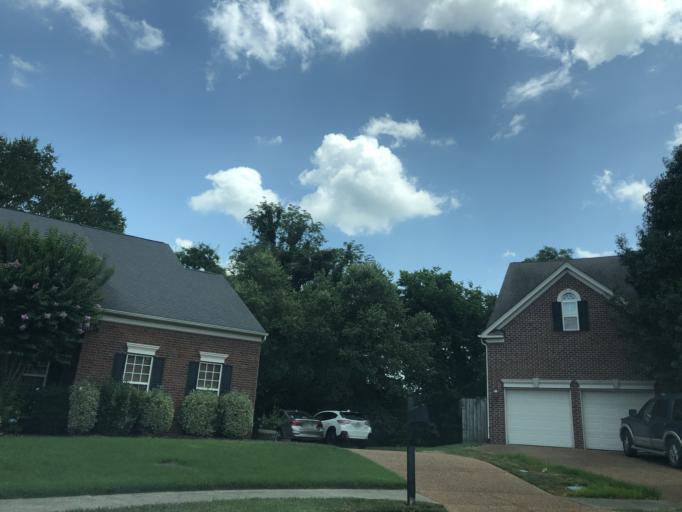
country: US
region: Tennessee
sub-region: Williamson County
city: Brentwood Estates
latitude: 36.0109
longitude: -86.7290
